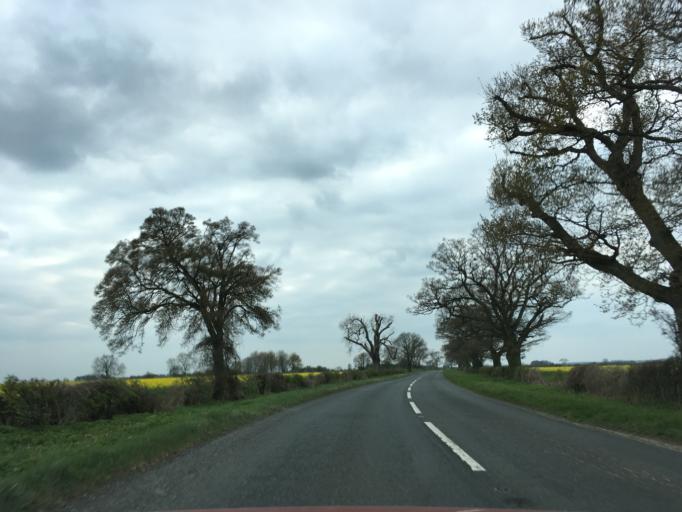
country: GB
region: England
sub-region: Gloucestershire
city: Northleach
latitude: 51.7726
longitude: -1.8050
